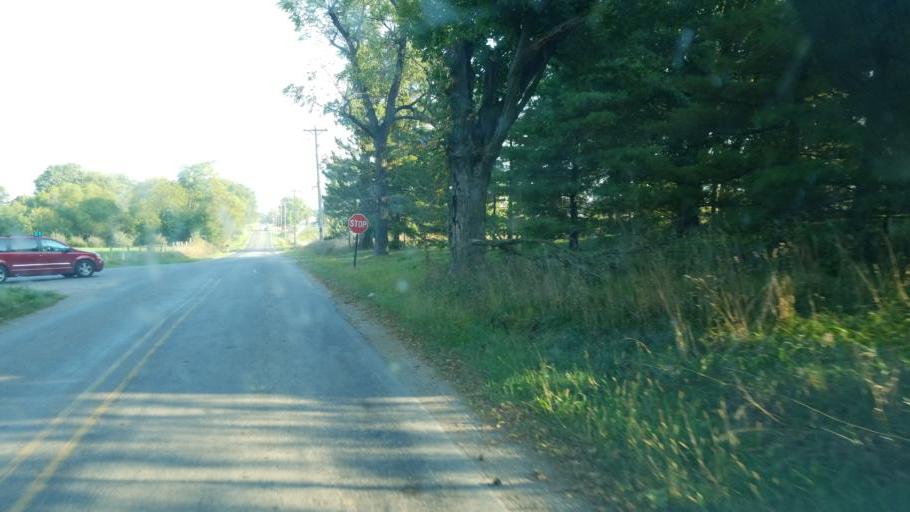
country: US
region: Indiana
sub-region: LaGrange County
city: Lagrange
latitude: 41.6231
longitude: -85.4245
